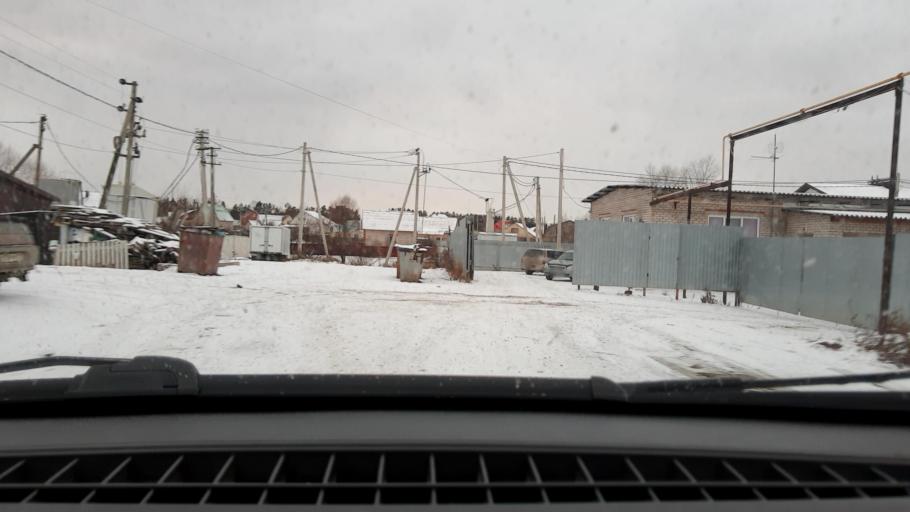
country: RU
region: Bashkortostan
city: Ufa
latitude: 54.7870
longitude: 55.9534
